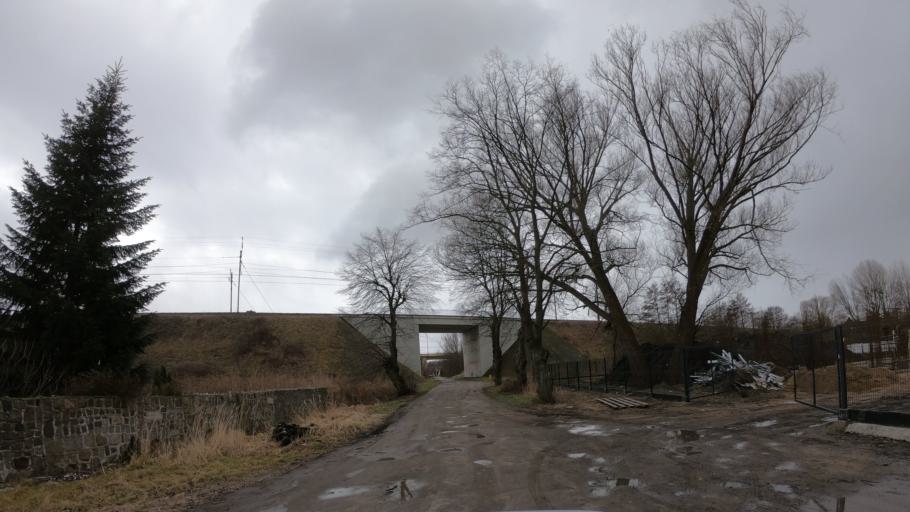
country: PL
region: West Pomeranian Voivodeship
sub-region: Powiat kamienski
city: Wolin
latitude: 53.8489
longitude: 14.6165
